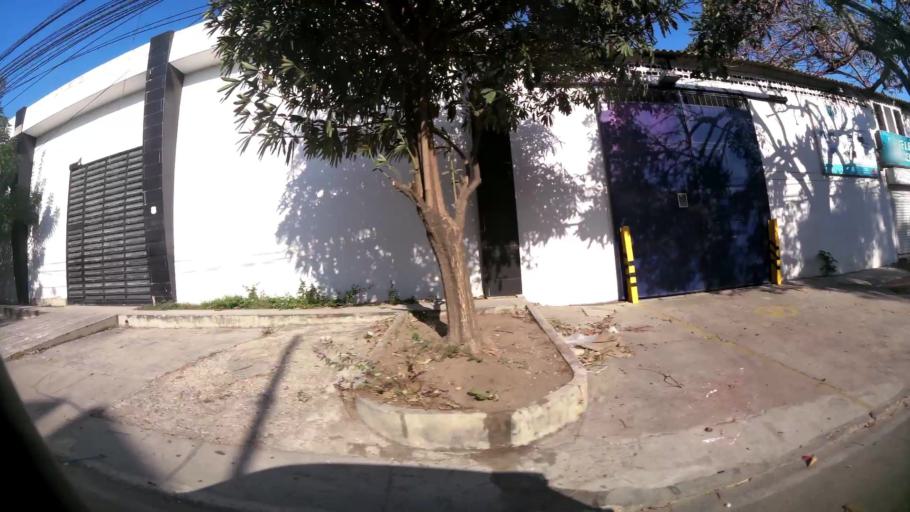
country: CO
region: Atlantico
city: Barranquilla
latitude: 11.0132
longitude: -74.7953
